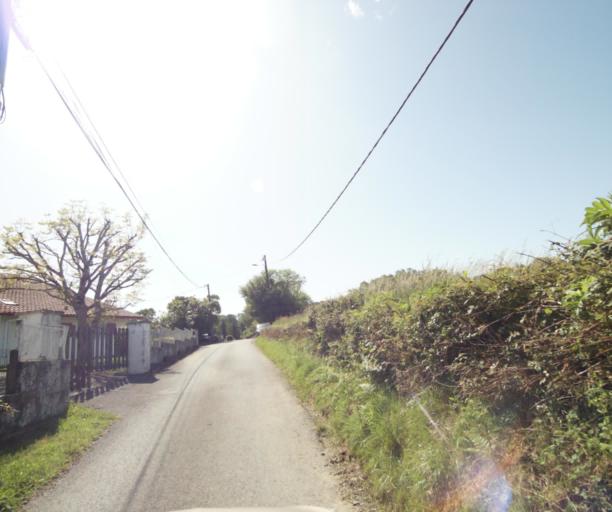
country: FR
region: Aquitaine
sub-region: Departement des Pyrenees-Atlantiques
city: Villefranque
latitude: 43.4618
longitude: -1.4458
